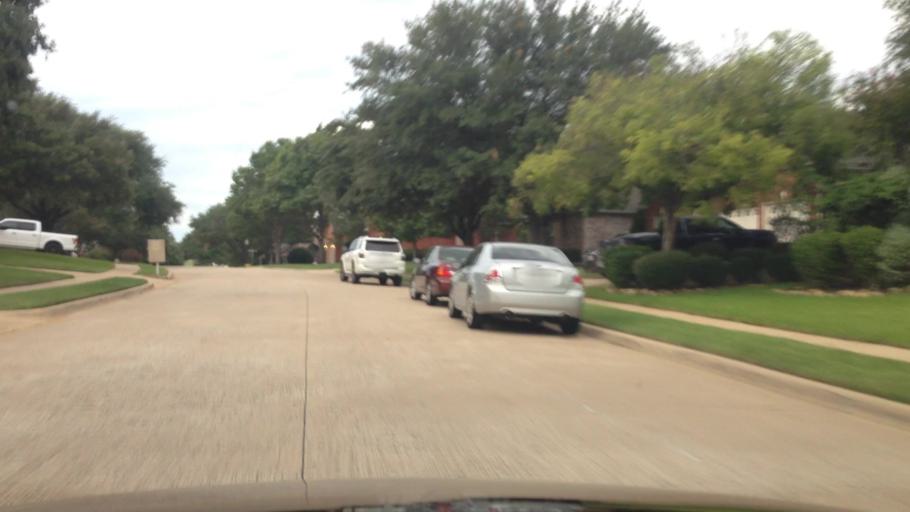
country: US
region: Texas
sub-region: Denton County
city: Flower Mound
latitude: 33.0036
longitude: -97.0488
